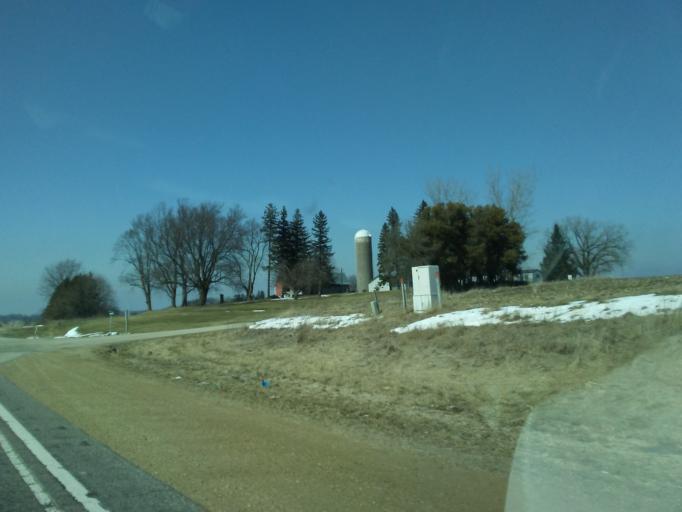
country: US
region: Wisconsin
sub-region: Vernon County
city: Westby
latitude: 43.6575
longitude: -90.9150
